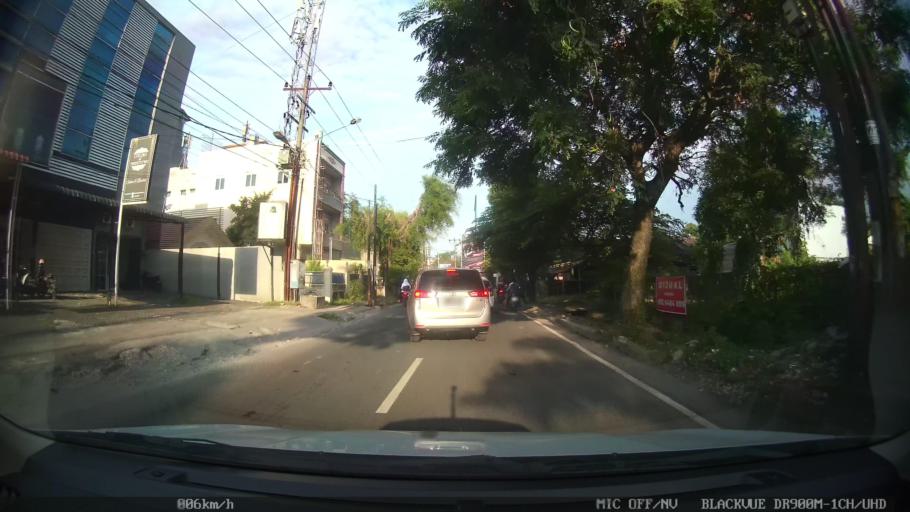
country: ID
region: North Sumatra
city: Medan
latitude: 3.5770
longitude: 98.6522
